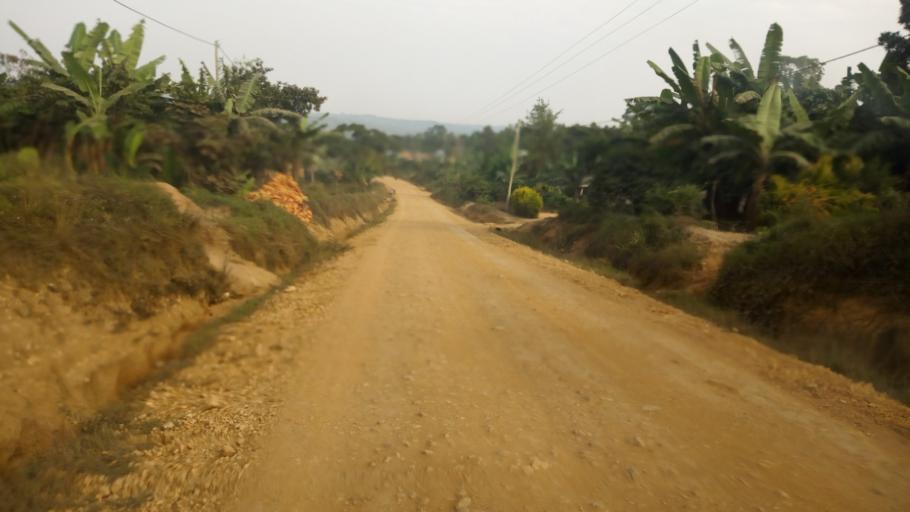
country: UG
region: Western Region
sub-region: Kanungu District
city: Ntungamo
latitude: -0.8405
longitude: 29.6541
